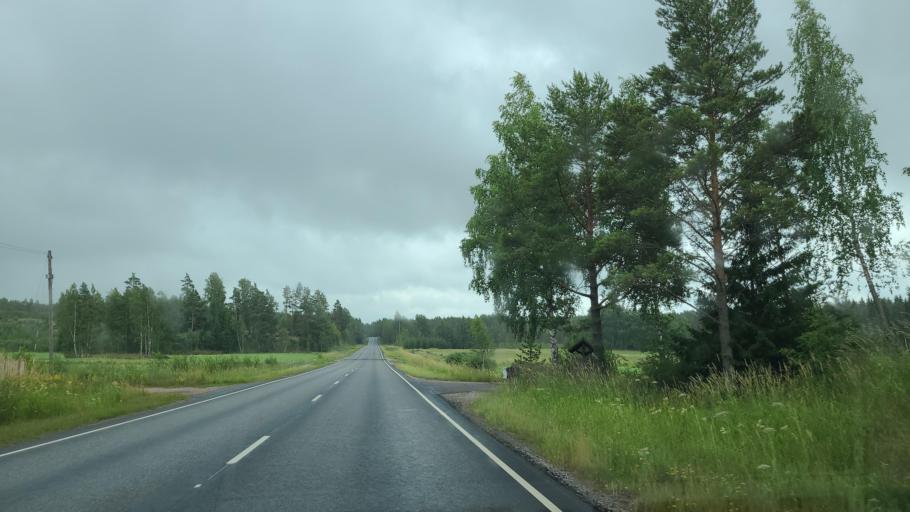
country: FI
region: Varsinais-Suomi
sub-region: Aboland-Turunmaa
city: Kimito
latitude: 60.2173
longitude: 22.6352
